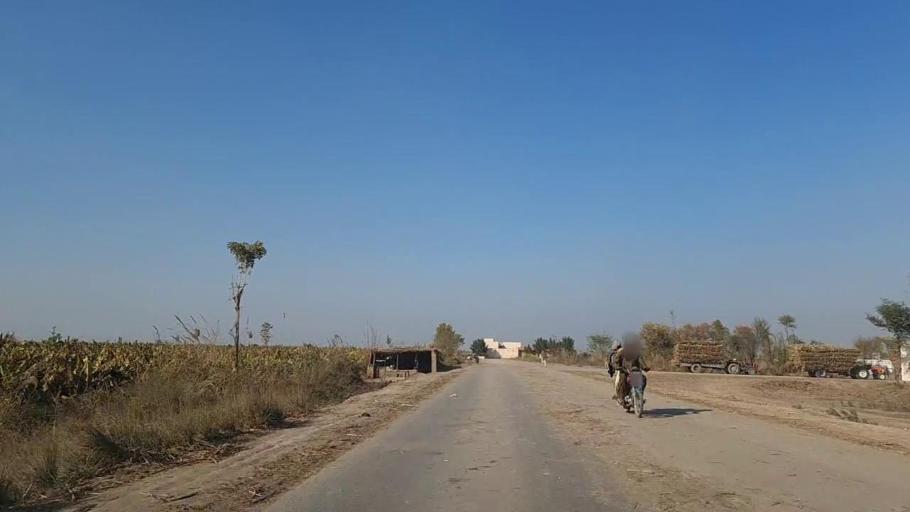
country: PK
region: Sindh
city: Bandhi
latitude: 26.6100
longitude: 68.3159
